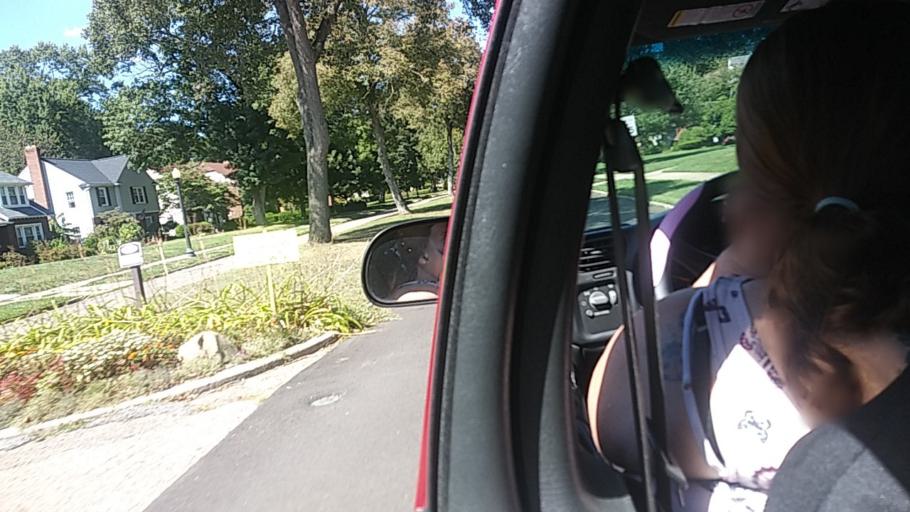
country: US
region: Ohio
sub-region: Summit County
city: Akron
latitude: 41.1087
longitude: -81.5614
